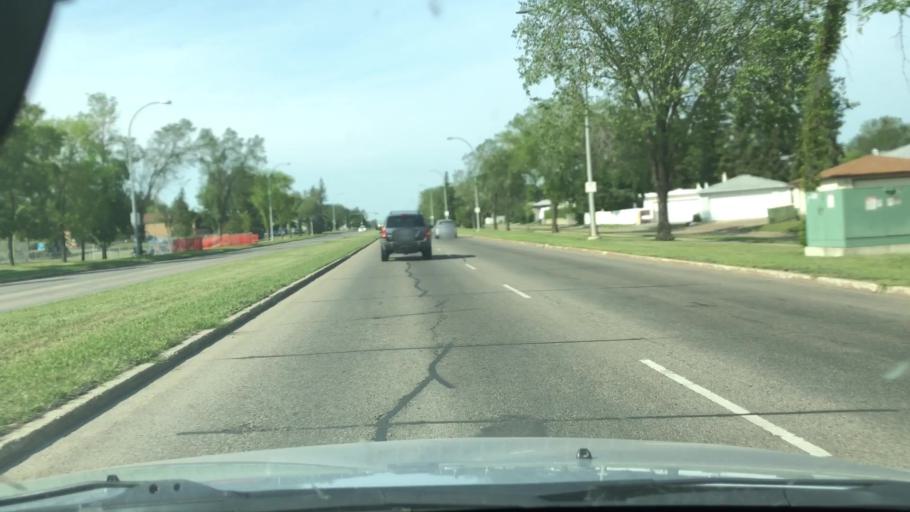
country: CA
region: Alberta
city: Edmonton
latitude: 53.6066
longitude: -113.4428
